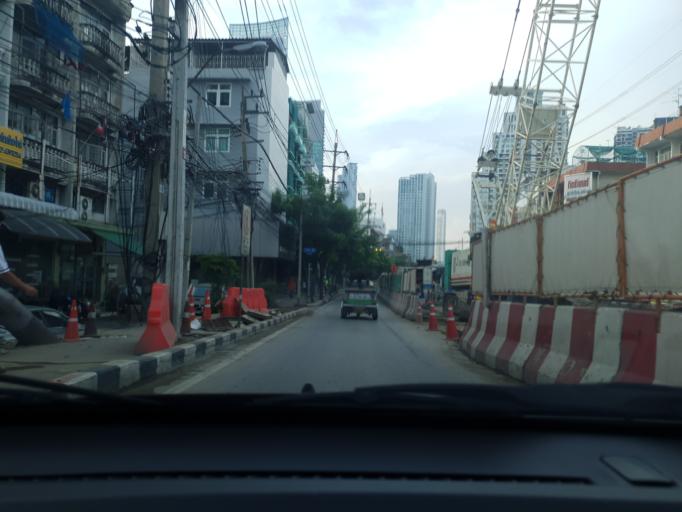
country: TH
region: Bangkok
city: Khlong San
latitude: 13.7257
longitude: 100.5092
